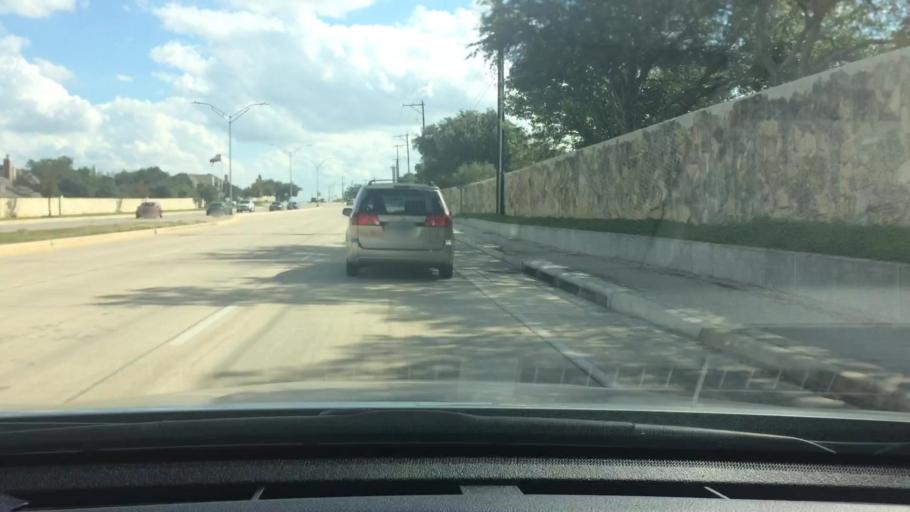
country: US
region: Texas
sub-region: Bexar County
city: Hollywood Park
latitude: 29.6135
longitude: -98.4216
